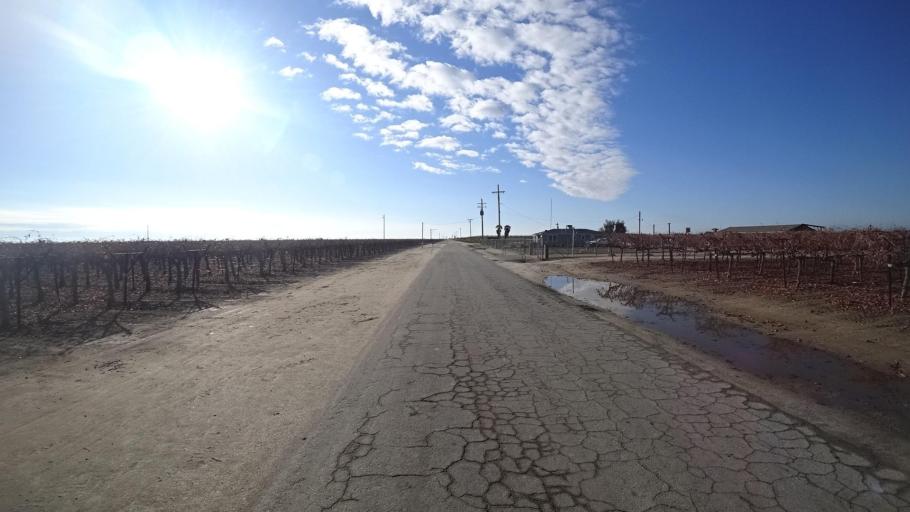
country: US
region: California
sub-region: Kern County
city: Delano
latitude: 35.7262
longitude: -119.3030
